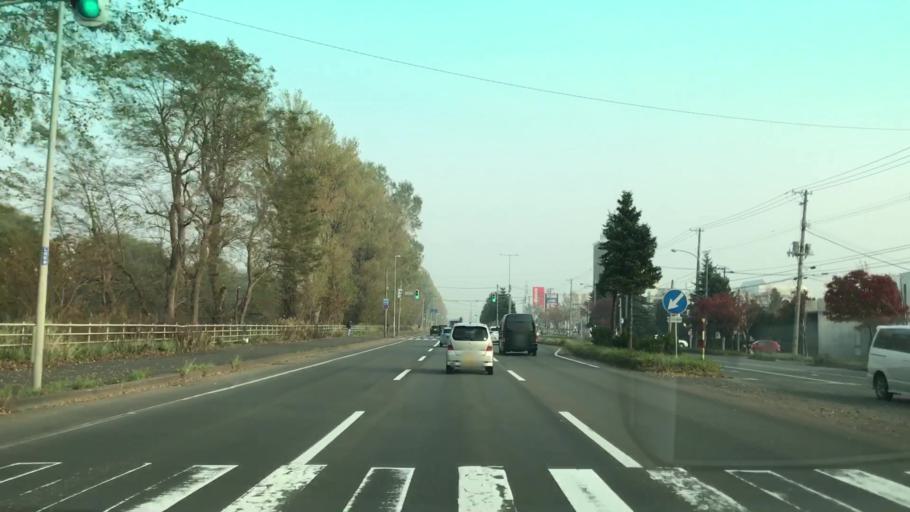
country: JP
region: Hokkaido
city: Sapporo
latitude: 43.1372
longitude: 141.3478
